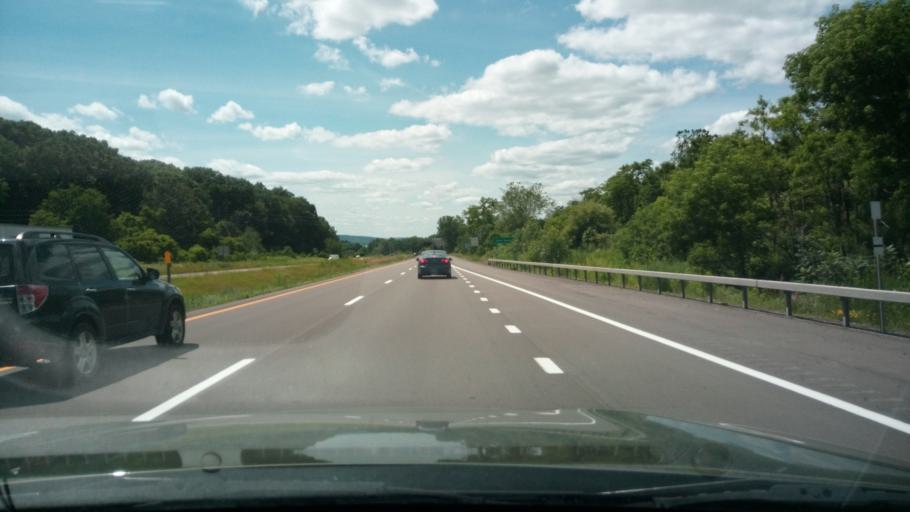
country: US
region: Pennsylvania
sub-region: Bradford County
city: South Waverly
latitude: 41.9998
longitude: -76.5507
